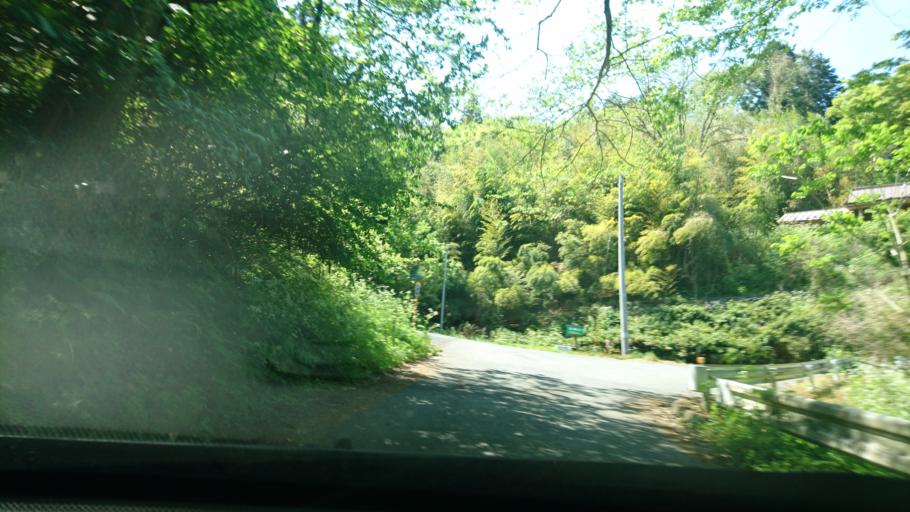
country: JP
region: Iwate
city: Ichinoseki
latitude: 38.9363
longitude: 141.2389
